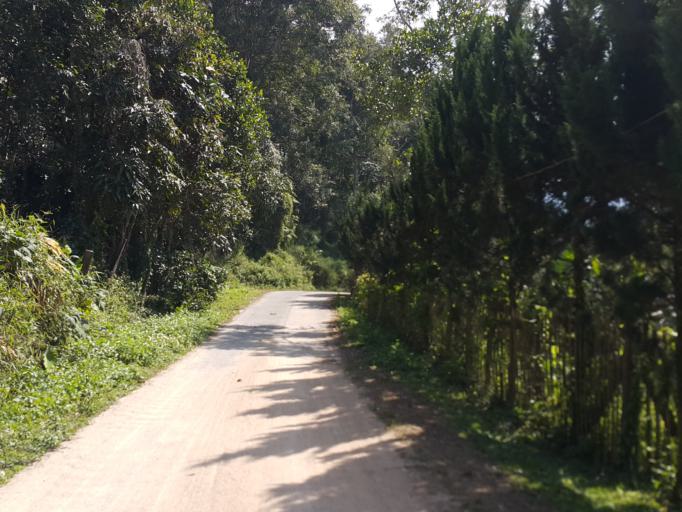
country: TH
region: Lampang
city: Wang Nuea
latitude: 19.0631
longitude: 99.3616
